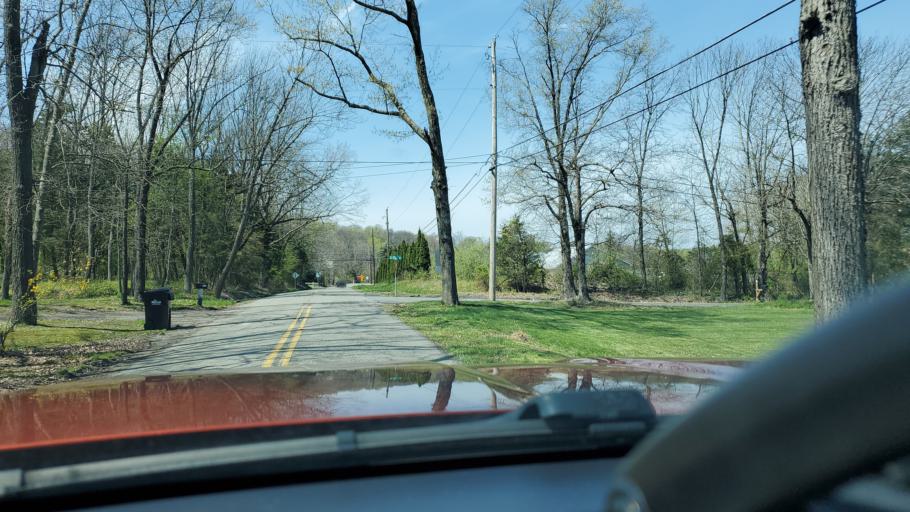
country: US
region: Pennsylvania
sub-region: Montgomery County
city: Gilbertsville
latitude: 40.3370
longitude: -75.5475
